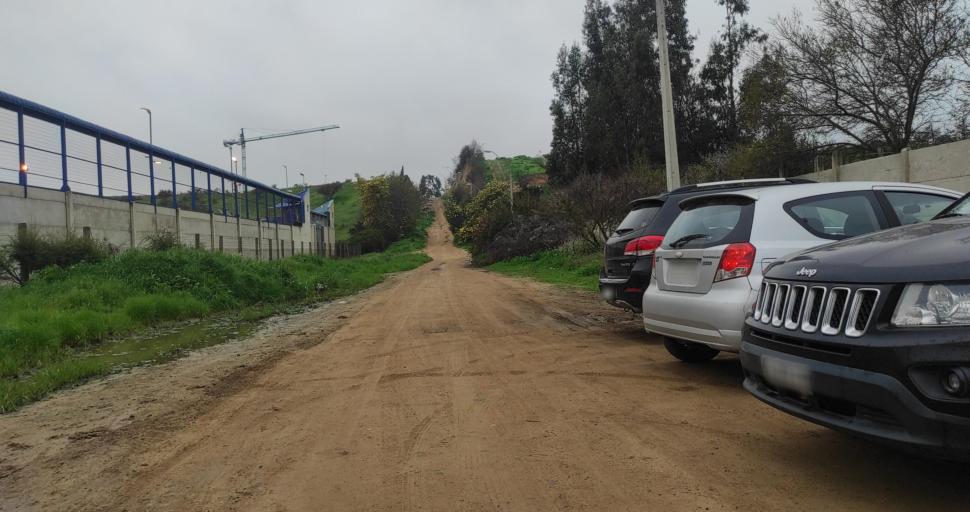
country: CL
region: Valparaiso
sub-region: Provincia de Marga Marga
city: Limache
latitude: -33.0210
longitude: -71.2622
